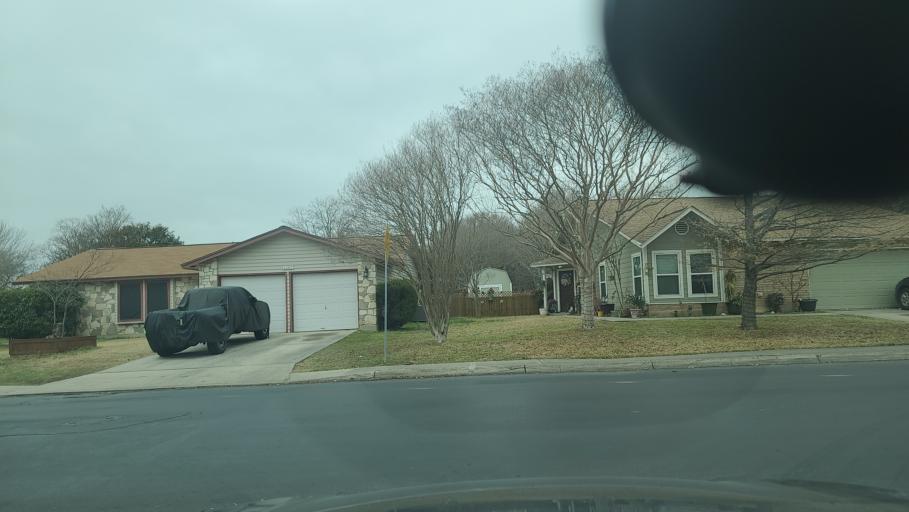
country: US
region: Texas
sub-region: Bexar County
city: Leon Valley
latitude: 29.5532
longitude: -98.6254
